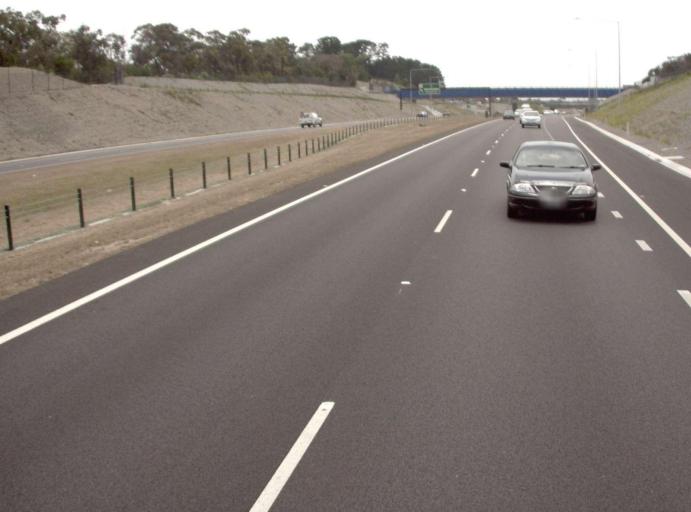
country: AU
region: Victoria
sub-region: Frankston
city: Langwarrin
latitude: -38.1622
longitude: 145.1659
